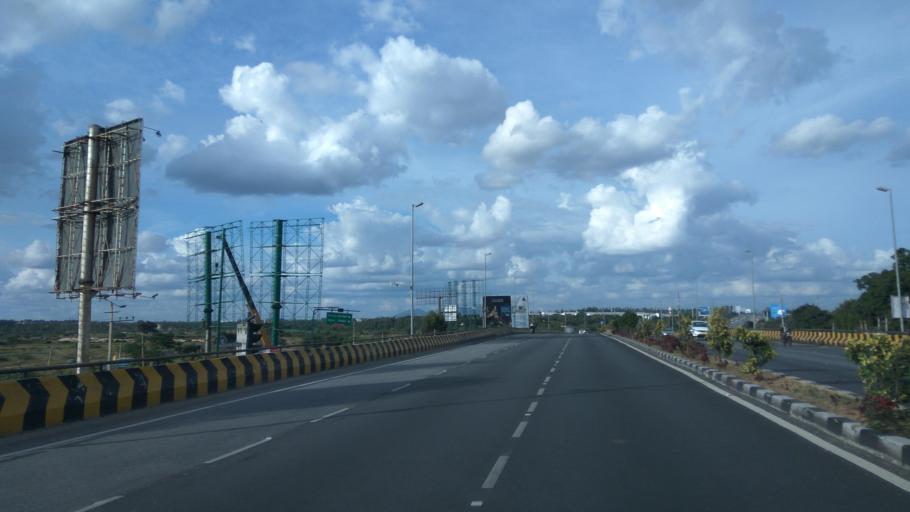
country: IN
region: Karnataka
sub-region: Bangalore Urban
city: Yelahanka
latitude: 13.1723
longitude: 77.6332
